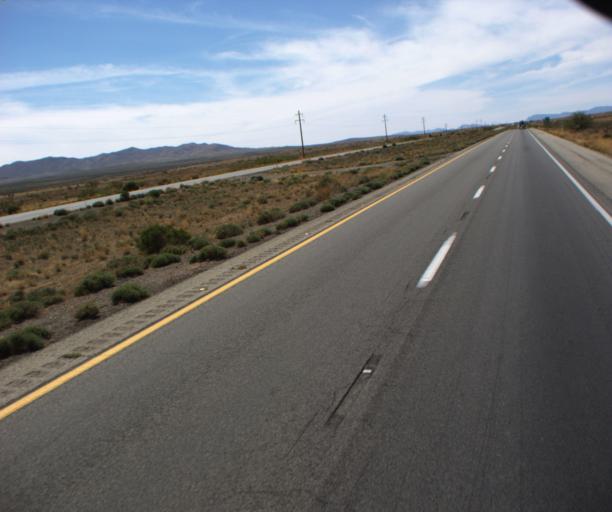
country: US
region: Arizona
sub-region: Cochise County
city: Willcox
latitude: 32.3622
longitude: -109.6529
